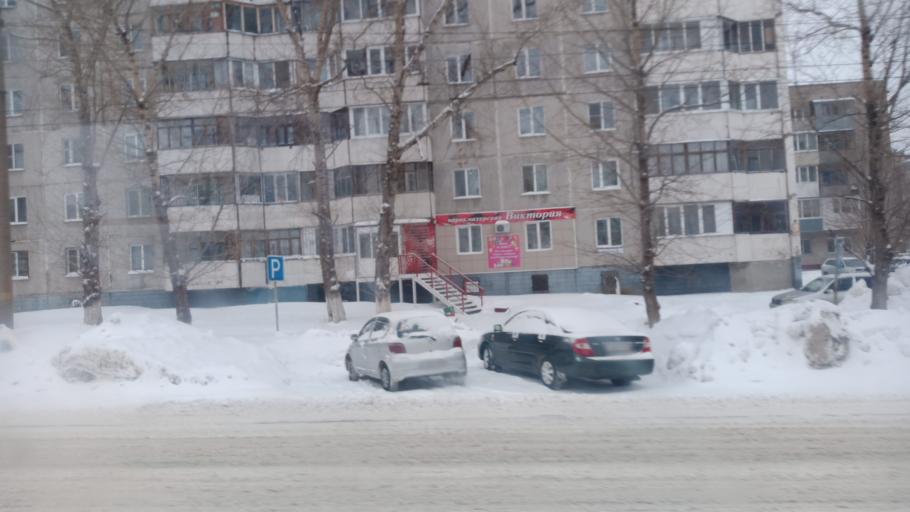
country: RU
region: Altai Krai
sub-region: Gorod Barnaulskiy
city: Barnaul
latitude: 53.3773
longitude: 83.7133
